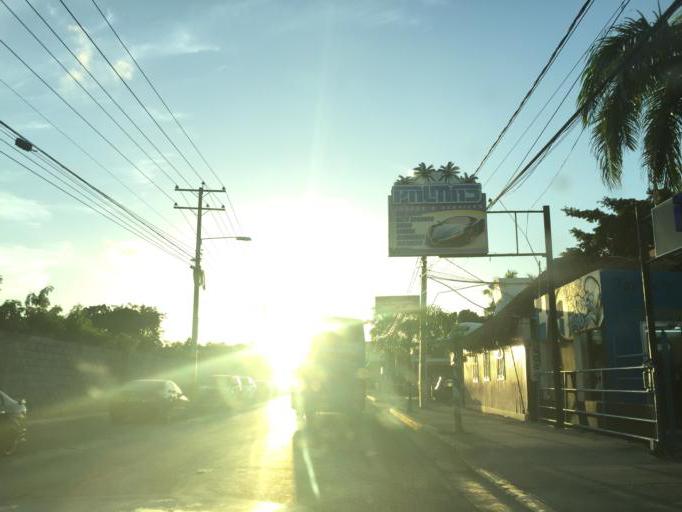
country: DO
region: San Juan
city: Punta Cana
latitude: 18.6865
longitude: -68.4471
